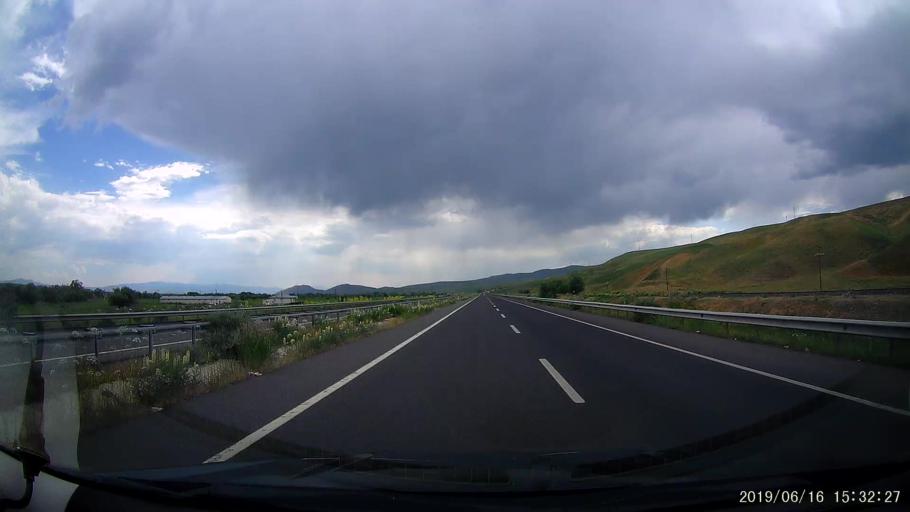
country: TR
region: Erzurum
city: Horasan
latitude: 40.0298
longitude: 42.0472
